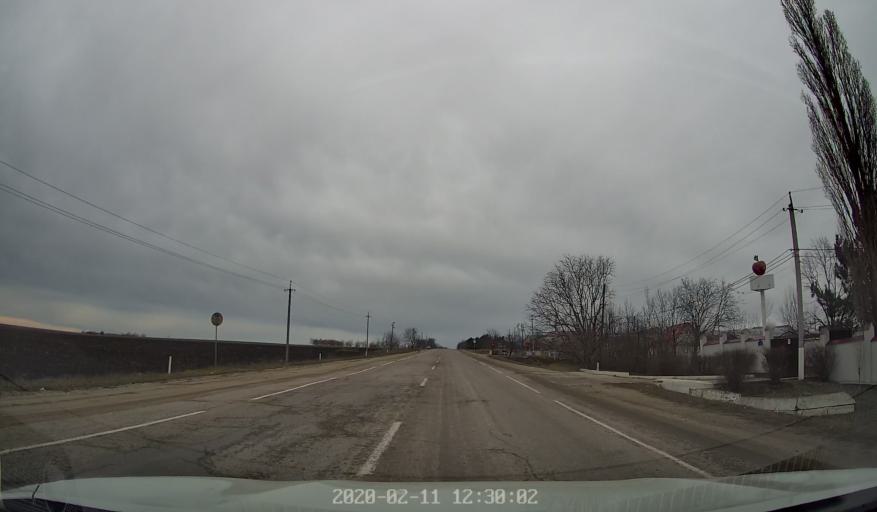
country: MD
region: Raionul Edinet
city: Edinet
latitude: 48.1589
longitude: 27.2869
